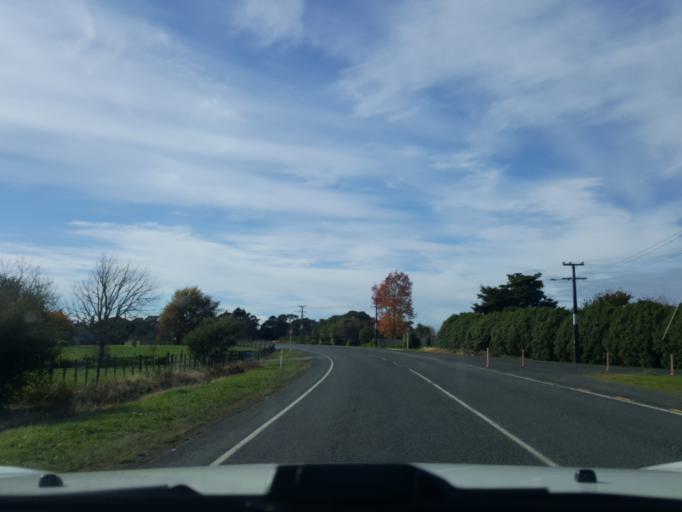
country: NZ
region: Waikato
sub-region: Waikato District
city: Ngaruawahia
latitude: -37.6097
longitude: 175.1948
